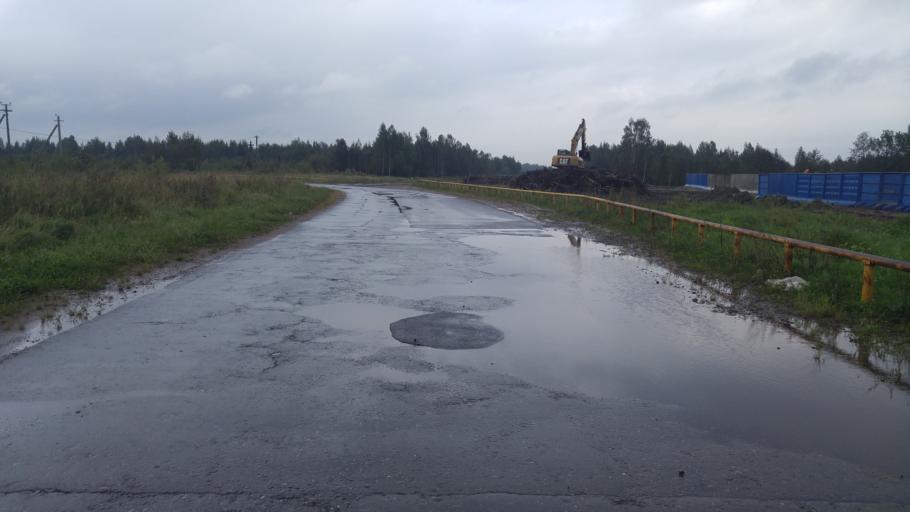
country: RU
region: St.-Petersburg
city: Ust'-Izhora
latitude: 59.7848
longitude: 30.5752
